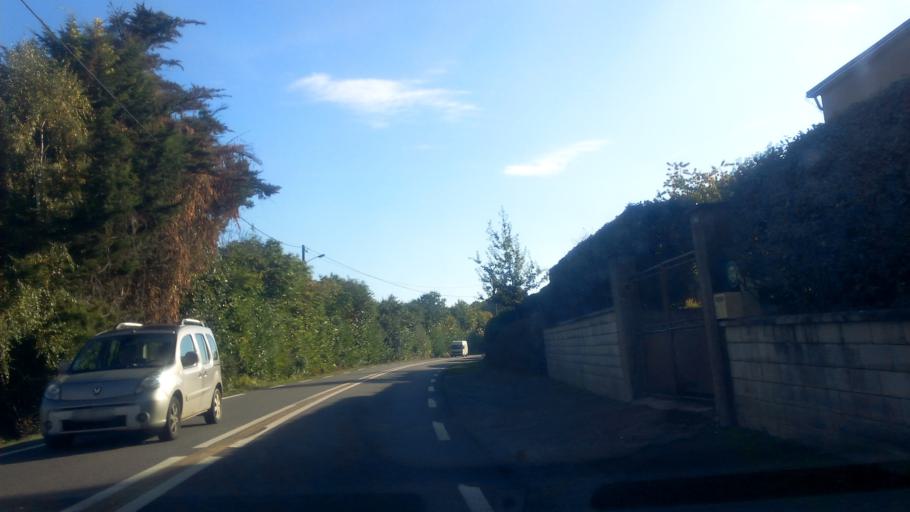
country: FR
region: Pays de la Loire
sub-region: Departement de la Loire-Atlantique
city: Saint-Nicolas-de-Redon
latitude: 47.6460
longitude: -2.0561
